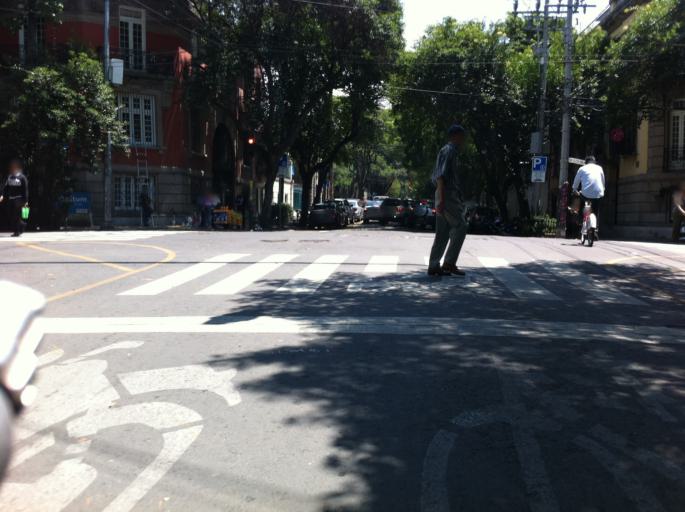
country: MX
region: Mexico City
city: Benito Juarez
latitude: 19.4195
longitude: -99.1630
